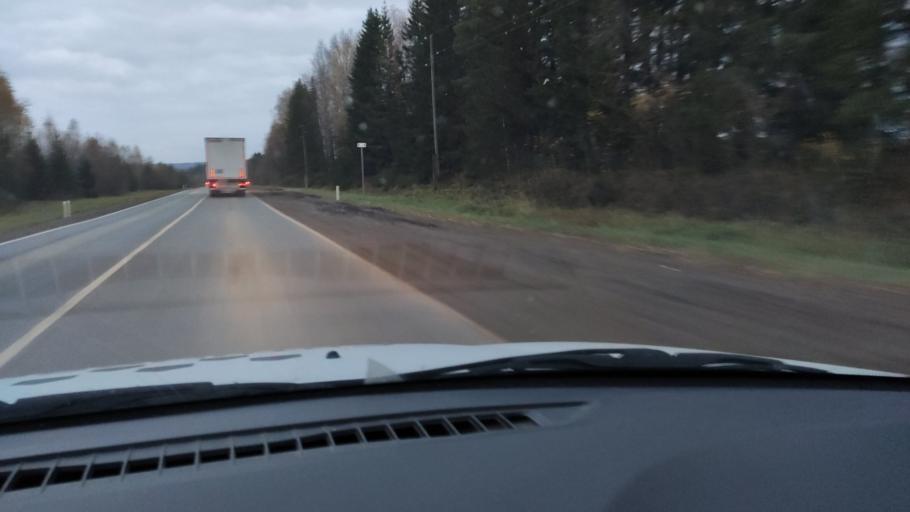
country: RU
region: Kirov
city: Kostino
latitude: 58.8572
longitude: 53.1873
